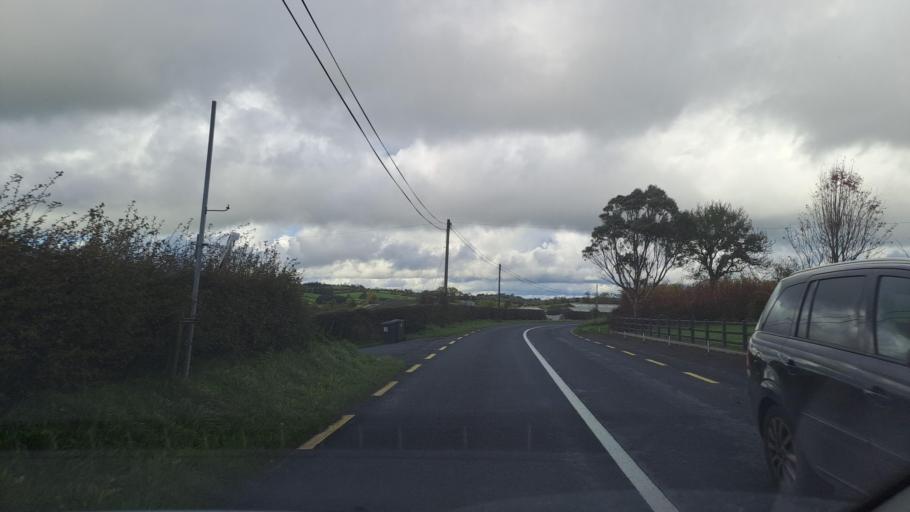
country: IE
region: Ulster
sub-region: An Cabhan
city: Bailieborough
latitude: 53.8752
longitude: -6.9664
